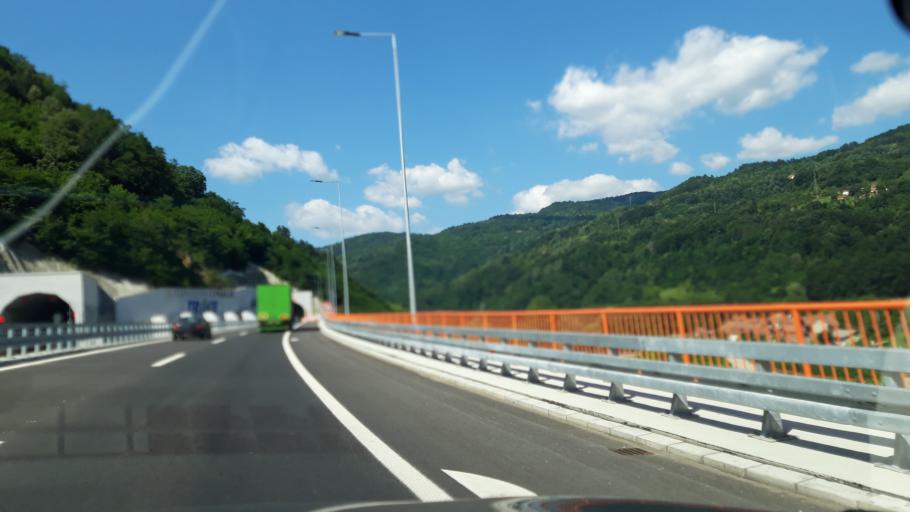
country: RS
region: Central Serbia
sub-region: Jablanicki Okrug
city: Vlasotince
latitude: 42.8338
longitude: 22.1286
